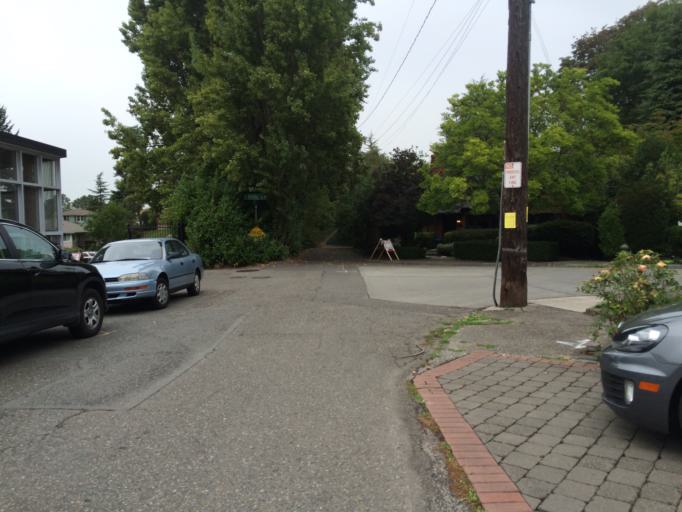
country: US
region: Washington
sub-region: King County
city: Seattle
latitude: 47.6385
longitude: -122.3073
